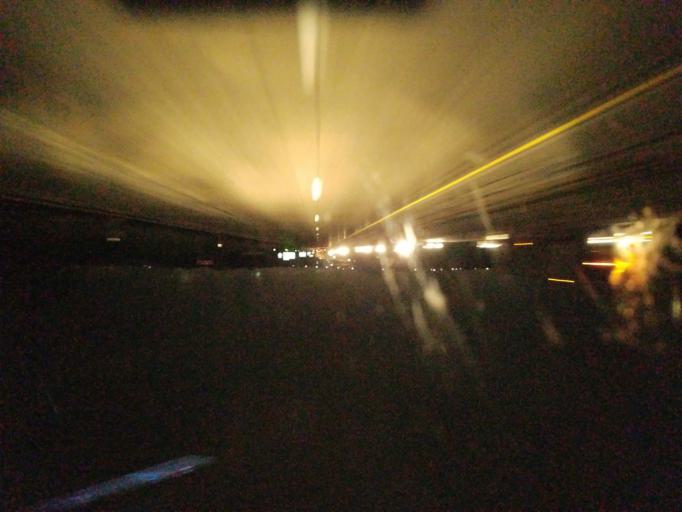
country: US
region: Iowa
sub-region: Dallas County
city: Waukee
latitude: 41.5635
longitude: -93.8754
